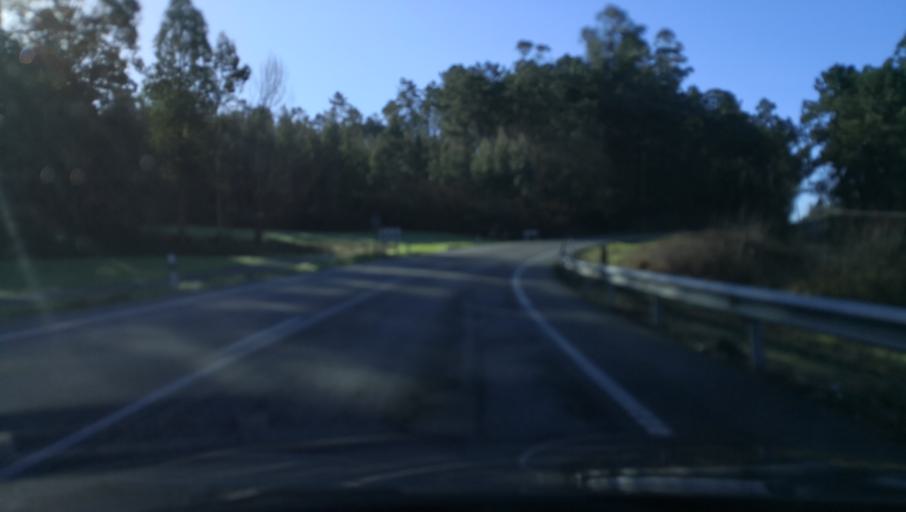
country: ES
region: Galicia
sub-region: Provincia da Coruna
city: Vedra
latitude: 42.8136
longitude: -8.4786
